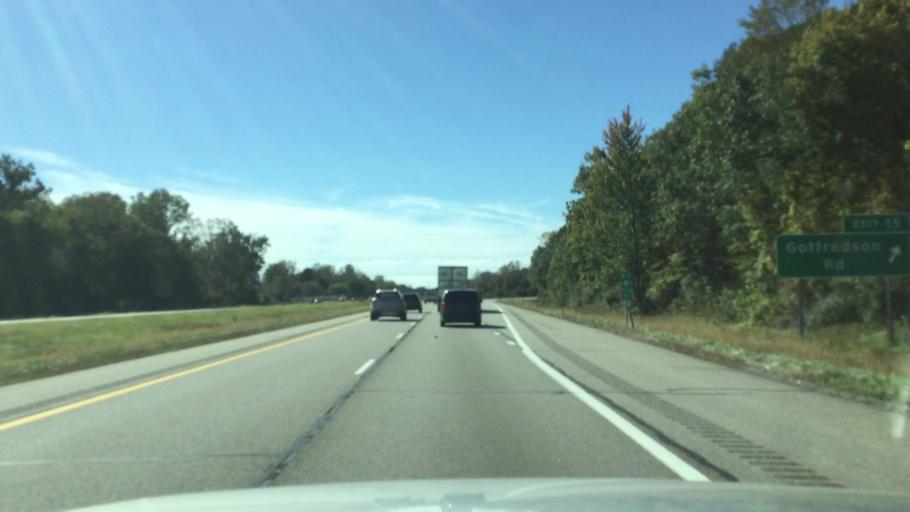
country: US
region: Michigan
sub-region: Wayne County
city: Plymouth
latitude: 42.3645
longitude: -83.5591
